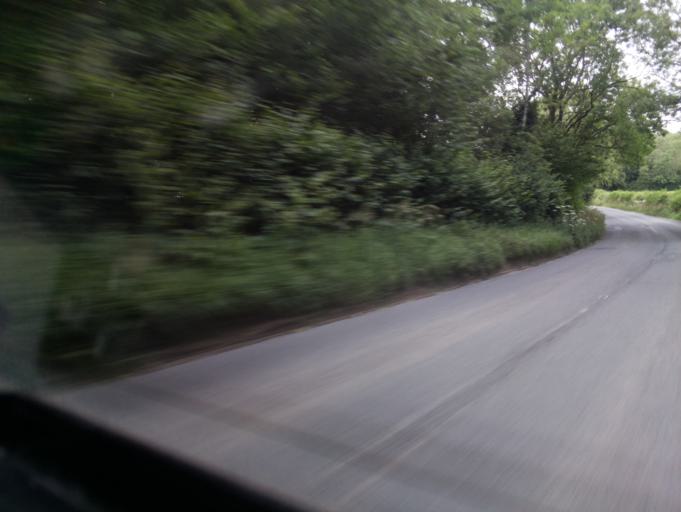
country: GB
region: England
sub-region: Gloucestershire
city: Chipping Campden
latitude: 51.9998
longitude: -1.7570
